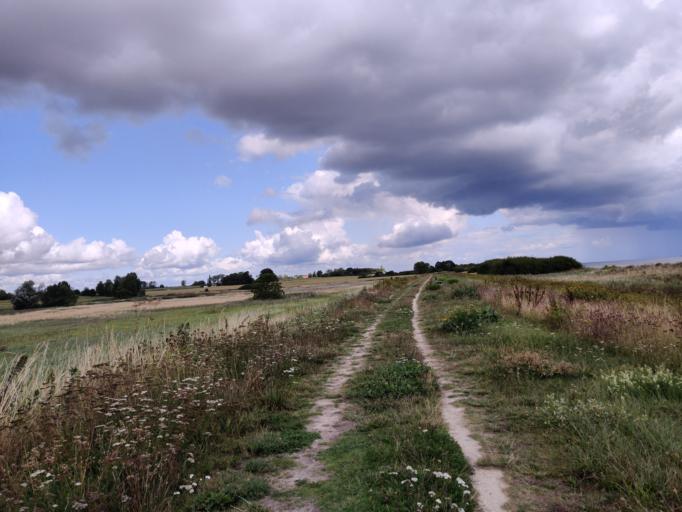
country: DK
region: Zealand
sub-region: Guldborgsund Kommune
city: Nykobing Falster
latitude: 54.7197
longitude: 12.0071
